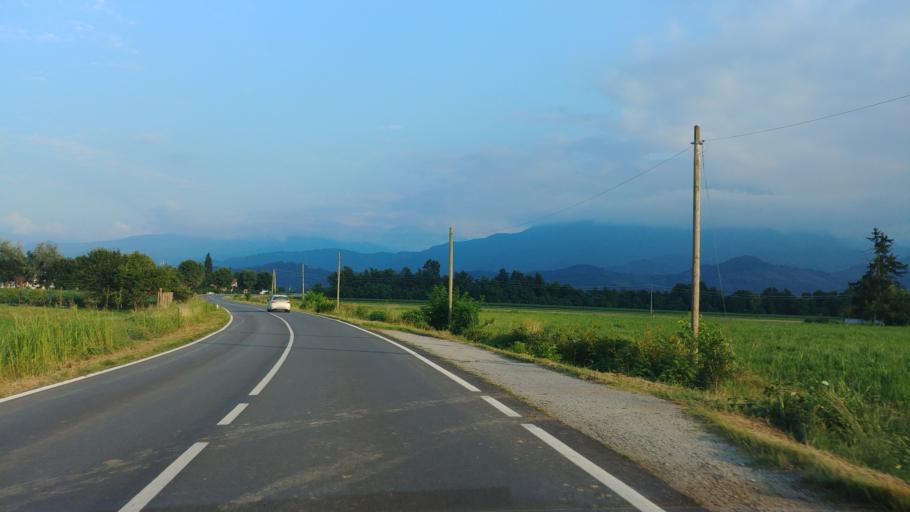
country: IT
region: Piedmont
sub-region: Provincia di Cuneo
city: Cuneo
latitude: 44.3618
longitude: 7.5861
